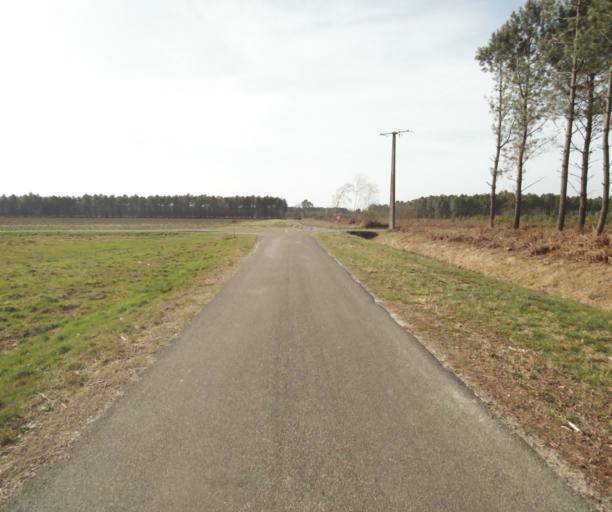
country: FR
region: Aquitaine
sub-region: Departement des Landes
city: Roquefort
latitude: 44.1450
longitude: -0.1598
